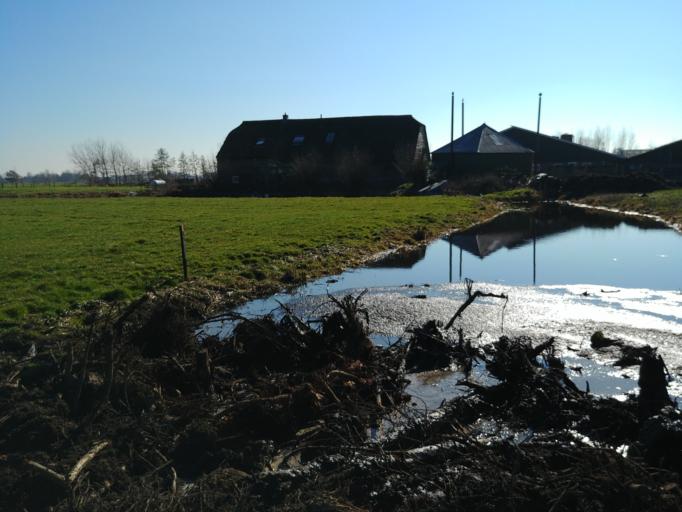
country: NL
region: Utrecht
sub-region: Gemeente Woerden
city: Woerden
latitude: 52.1260
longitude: 4.8821
